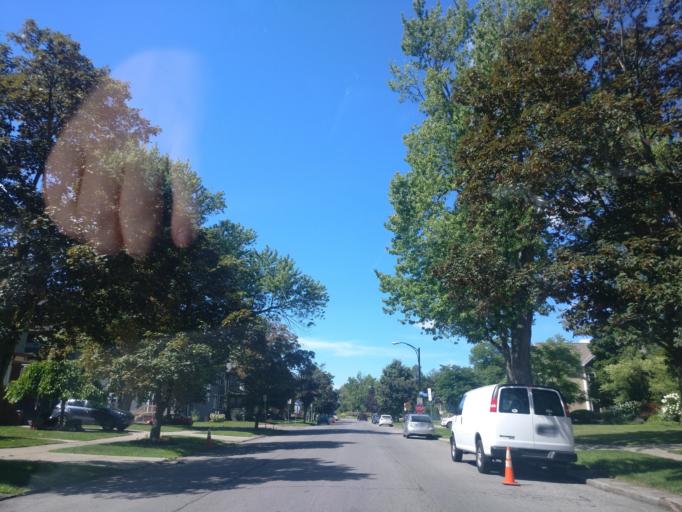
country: US
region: New York
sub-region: Erie County
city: Buffalo
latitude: 42.9155
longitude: -78.8796
